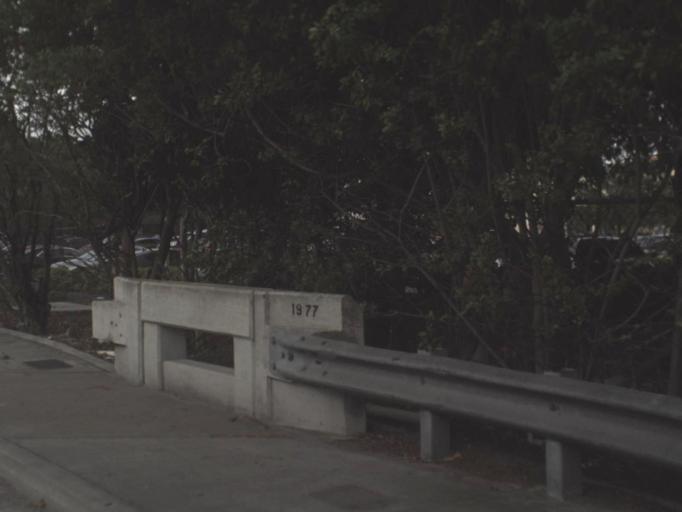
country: US
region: Florida
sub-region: Miami-Dade County
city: Doral
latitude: 25.8103
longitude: -80.3388
